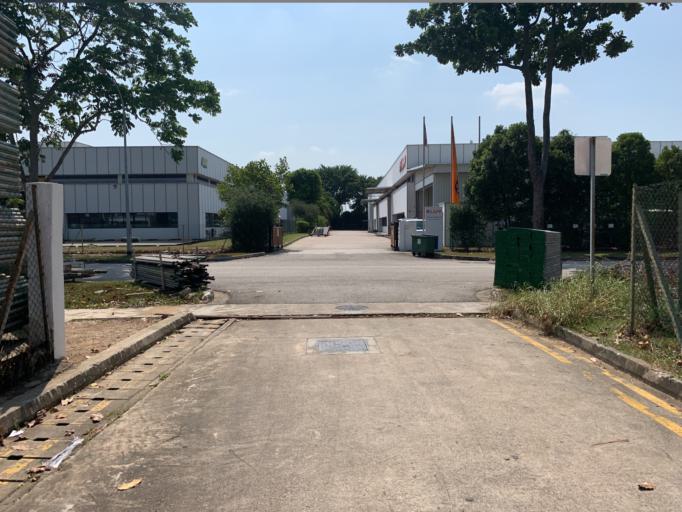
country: MY
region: Johor
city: Johor Bahru
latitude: 1.3057
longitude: 103.6295
